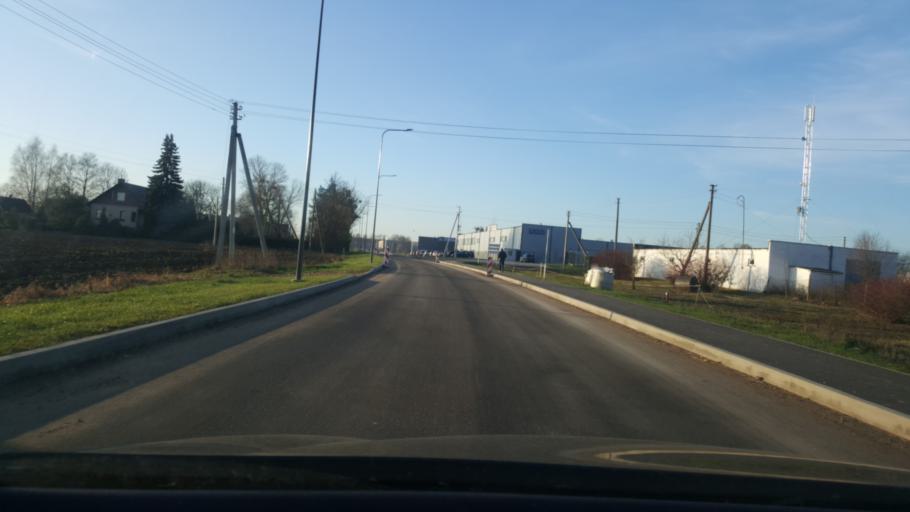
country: LT
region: Kauno apskritis
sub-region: Kauno rajonas
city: Mastaiciai
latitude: 54.8552
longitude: 23.8502
